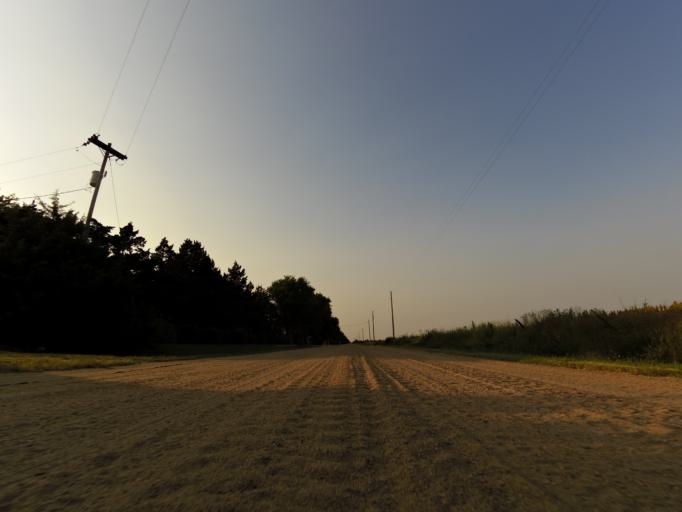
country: US
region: Kansas
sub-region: Reno County
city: South Hutchinson
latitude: 37.9860
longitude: -97.9957
